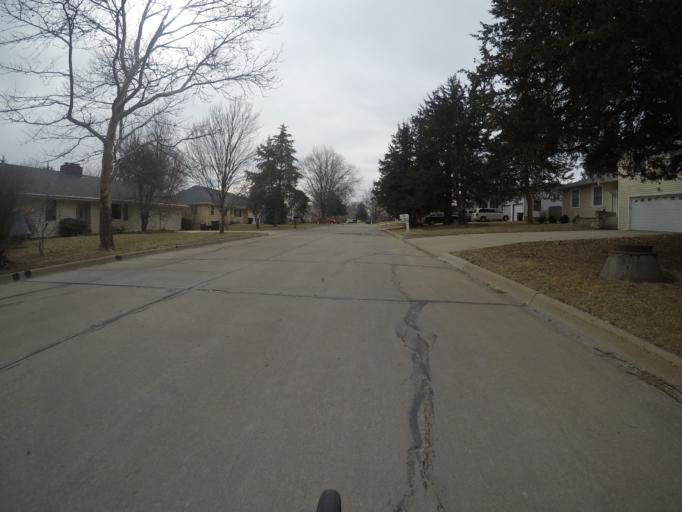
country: US
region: Kansas
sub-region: Riley County
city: Manhattan
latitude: 39.1978
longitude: -96.6231
